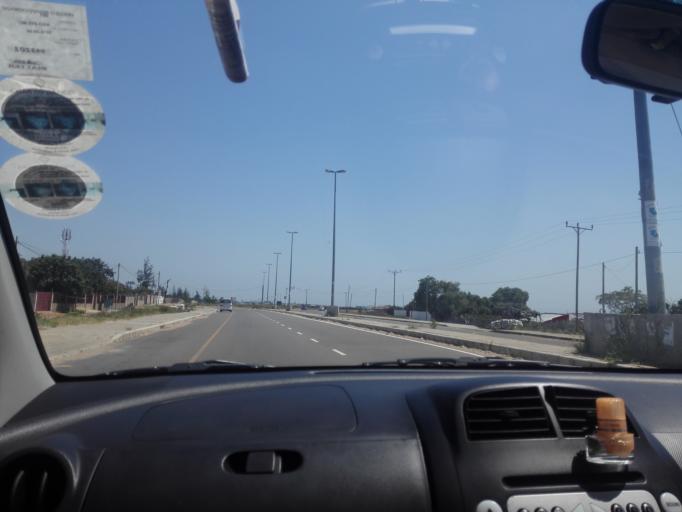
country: MZ
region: Maputo City
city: Maputo
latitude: -25.8503
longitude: 32.6713
